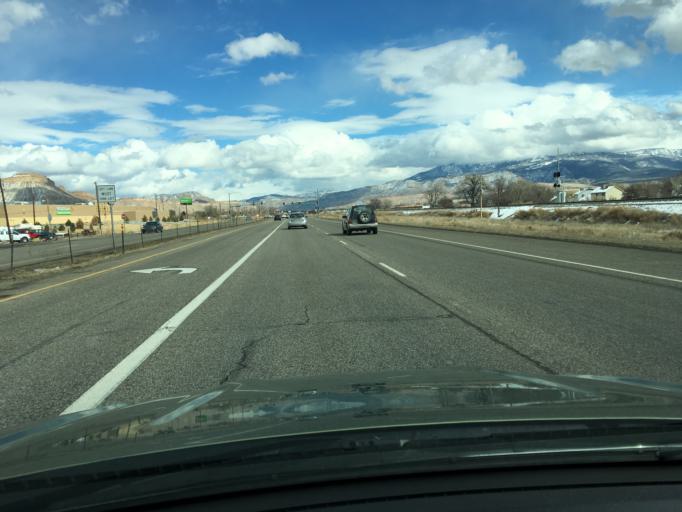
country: US
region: Colorado
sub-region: Mesa County
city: Fruitvale
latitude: 39.0821
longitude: -108.4760
